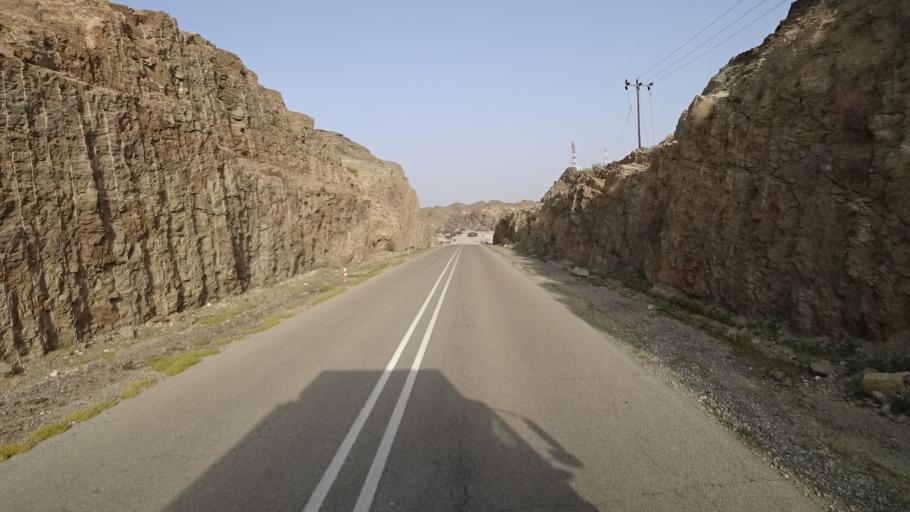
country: OM
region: Muhafazat Masqat
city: Bawshar
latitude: 23.3579
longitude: 58.5296
